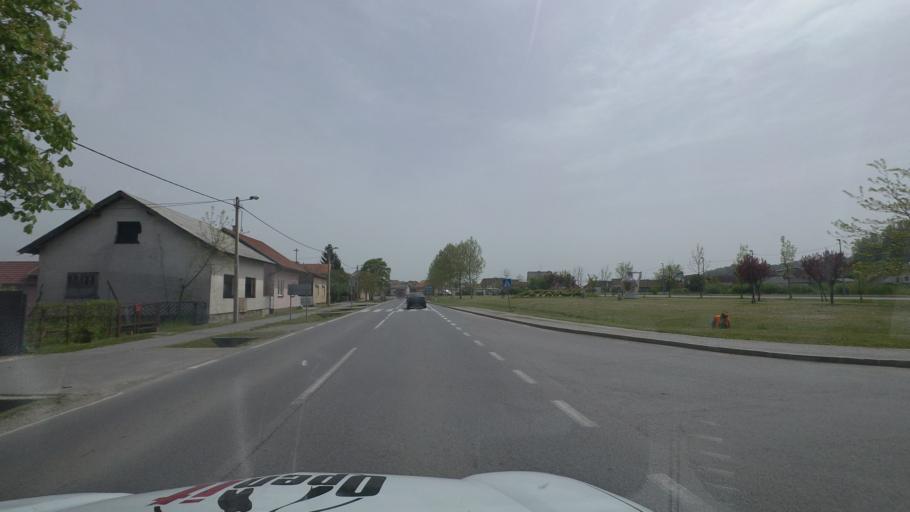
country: HR
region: Sisacko-Moslavacka
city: Petrinja
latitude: 45.4383
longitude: 16.2605
